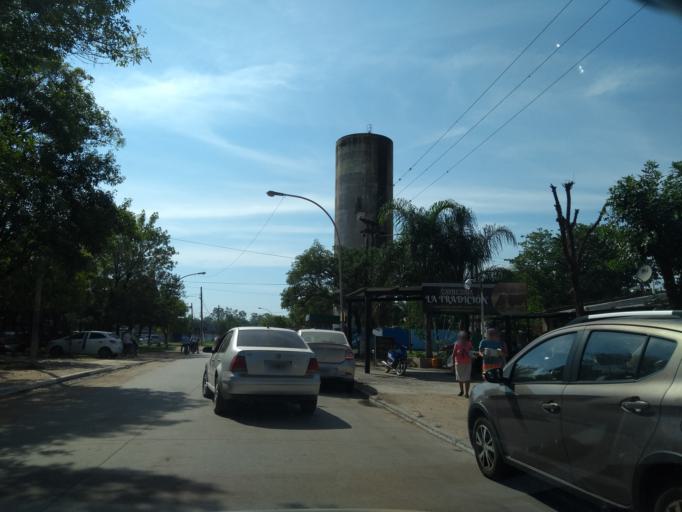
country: AR
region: Chaco
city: Barranqueras
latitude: -27.4646
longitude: -58.9495
